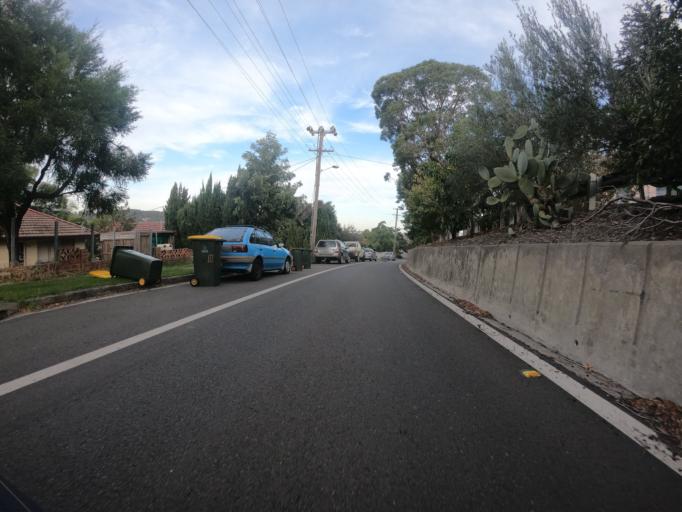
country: AU
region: New South Wales
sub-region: Wollongong
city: West Wollongong
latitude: -34.4313
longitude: 150.8589
